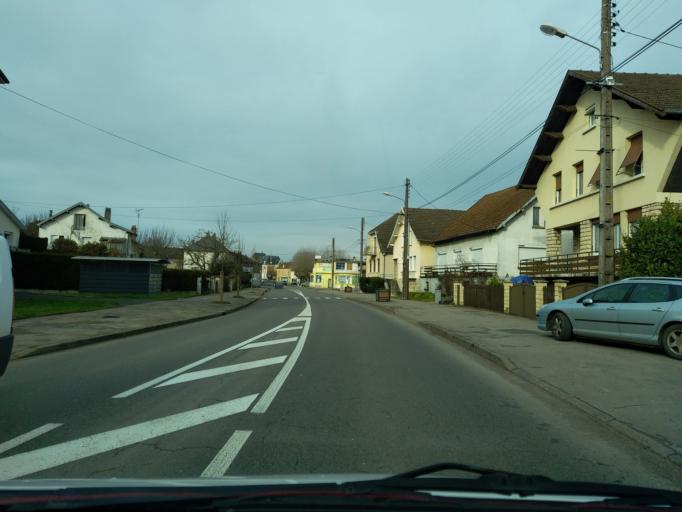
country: FR
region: Franche-Comte
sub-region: Departement de la Haute-Saone
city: Gray
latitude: 47.4468
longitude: 5.5972
